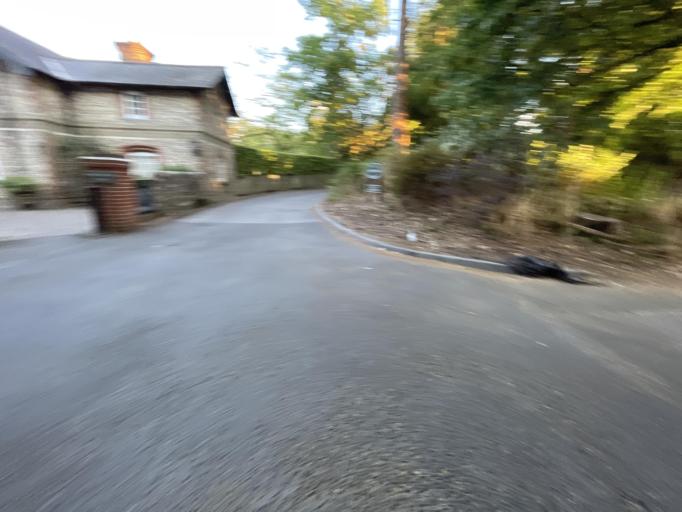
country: GB
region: England
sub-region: Surrey
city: East Horsley
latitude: 51.2708
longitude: -0.4272
